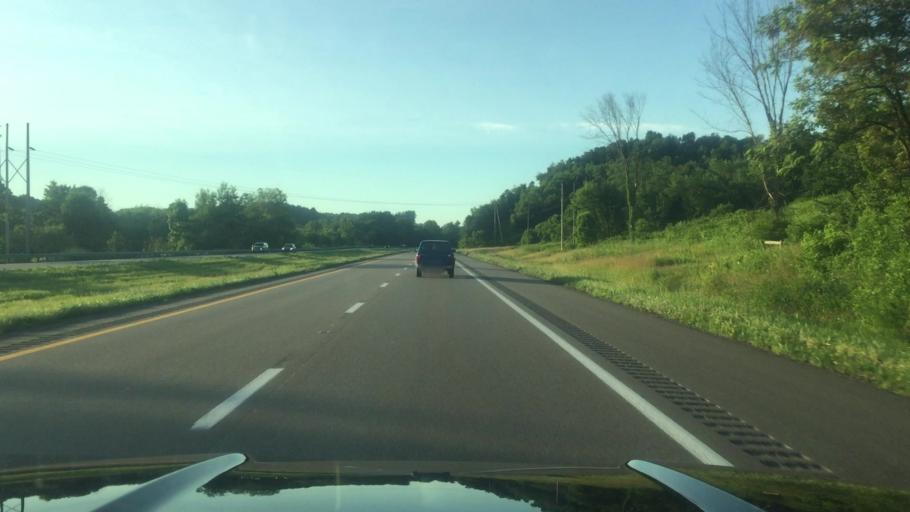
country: US
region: Ohio
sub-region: Tuscarawas County
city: Newcomerstown
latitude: 40.3335
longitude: -81.5699
